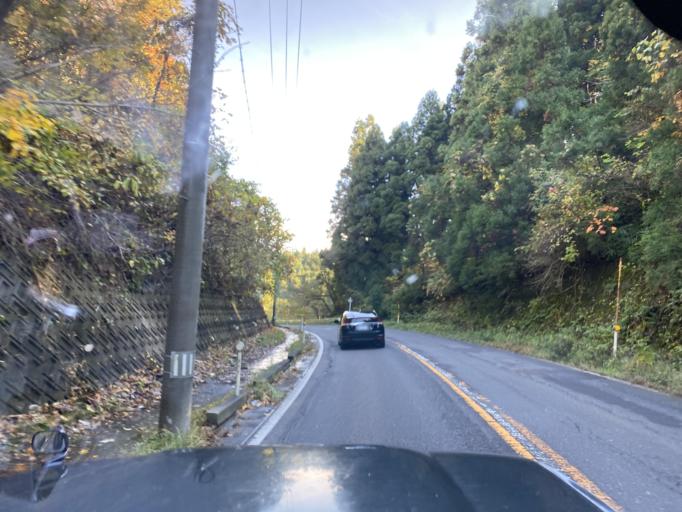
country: JP
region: Niigata
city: Niitsu-honcho
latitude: 37.7491
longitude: 139.1087
